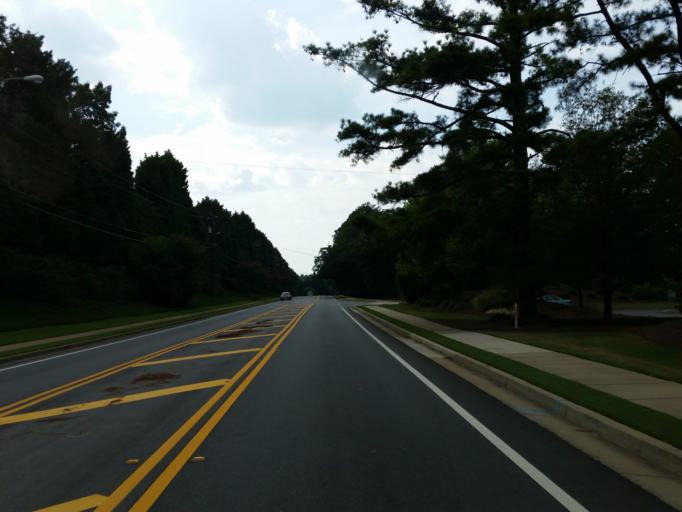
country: US
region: Georgia
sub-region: Fulton County
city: Roswell
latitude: 34.0488
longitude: -84.3787
